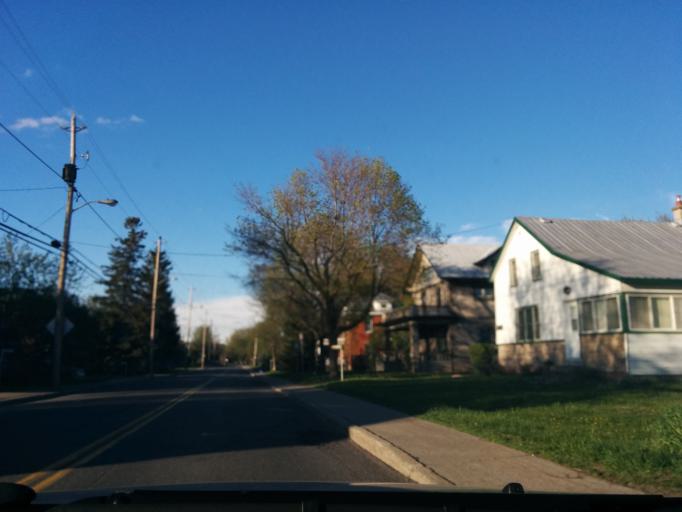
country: CA
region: Ontario
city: Bells Corners
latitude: 45.1413
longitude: -75.6143
